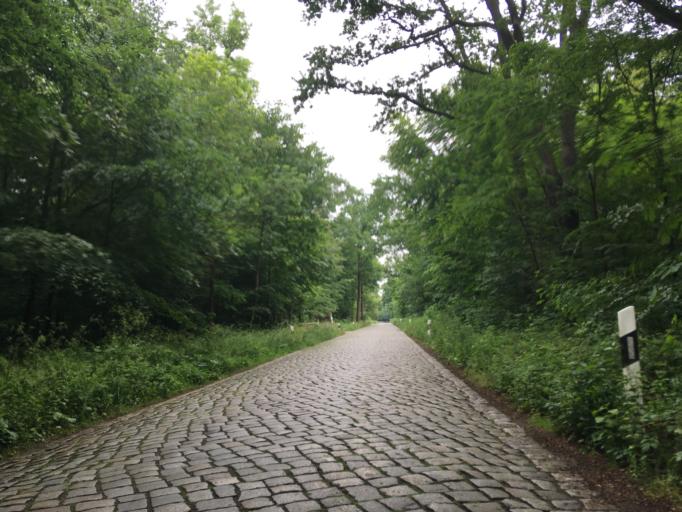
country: DE
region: Berlin
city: Buch
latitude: 52.6517
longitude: 13.4856
